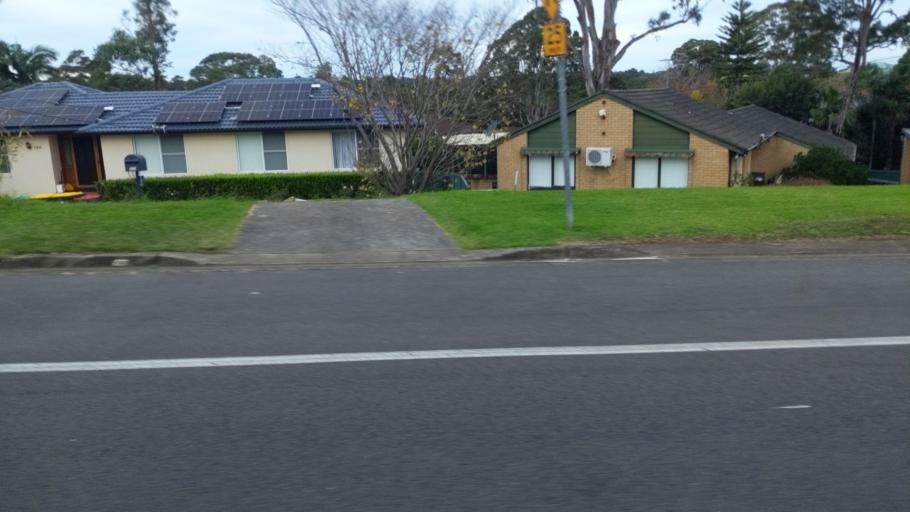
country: AU
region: New South Wales
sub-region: The Hills Shire
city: Baulkham Hills
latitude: -33.7532
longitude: 150.9607
